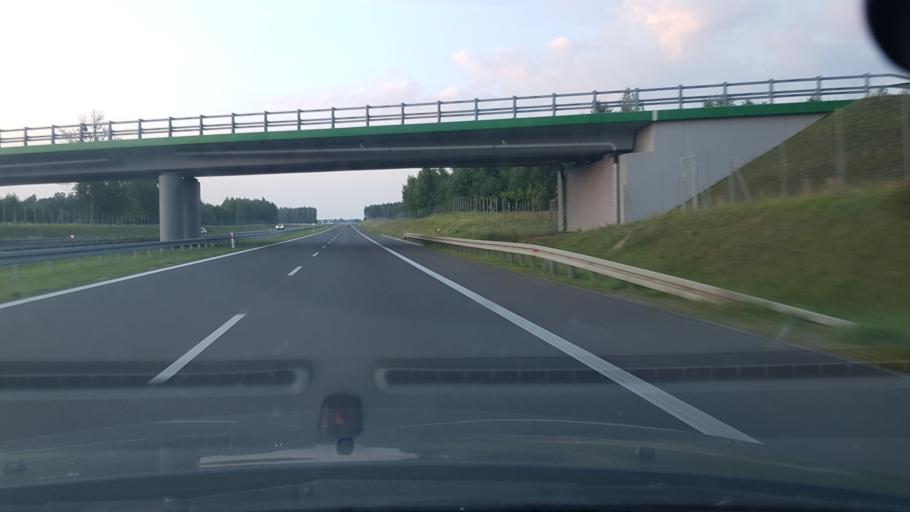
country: PL
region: Masovian Voivodeship
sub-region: Powiat mlawski
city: Wieczfnia Koscielna
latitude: 53.2625
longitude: 20.4284
